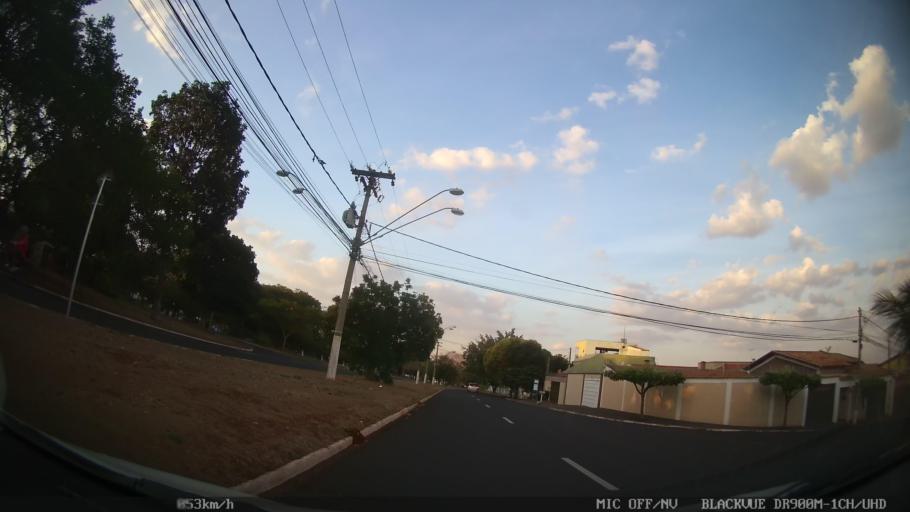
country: BR
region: Sao Paulo
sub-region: Ribeirao Preto
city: Ribeirao Preto
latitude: -21.1365
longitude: -47.8479
